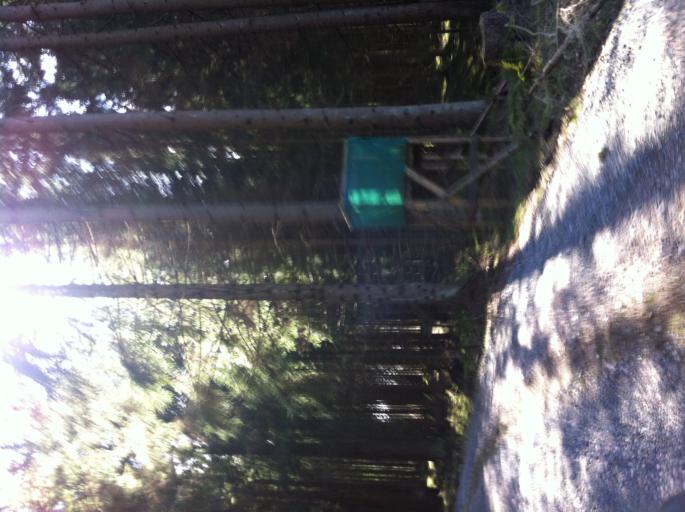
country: SE
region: Skane
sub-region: Hoors Kommun
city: Hoeoer
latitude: 56.0006
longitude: 13.5681
